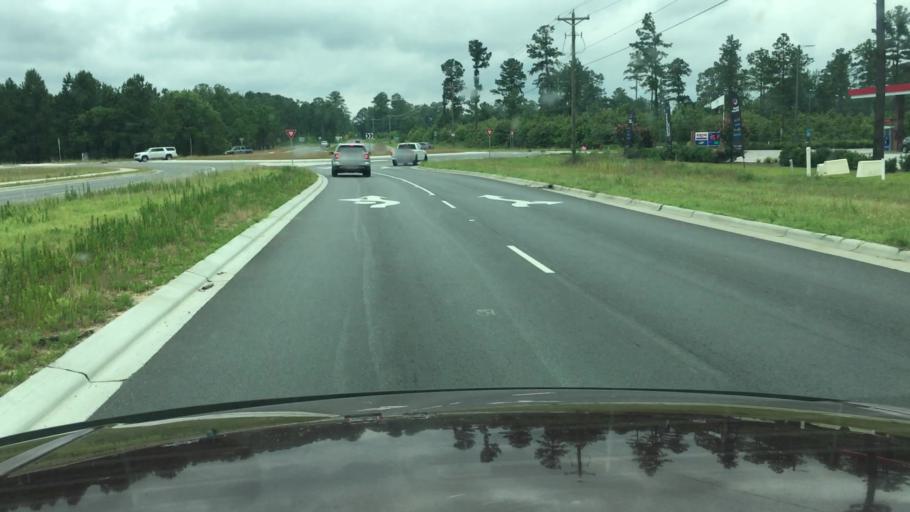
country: US
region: North Carolina
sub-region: Cumberland County
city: Spring Lake
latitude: 35.2580
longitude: -78.9695
